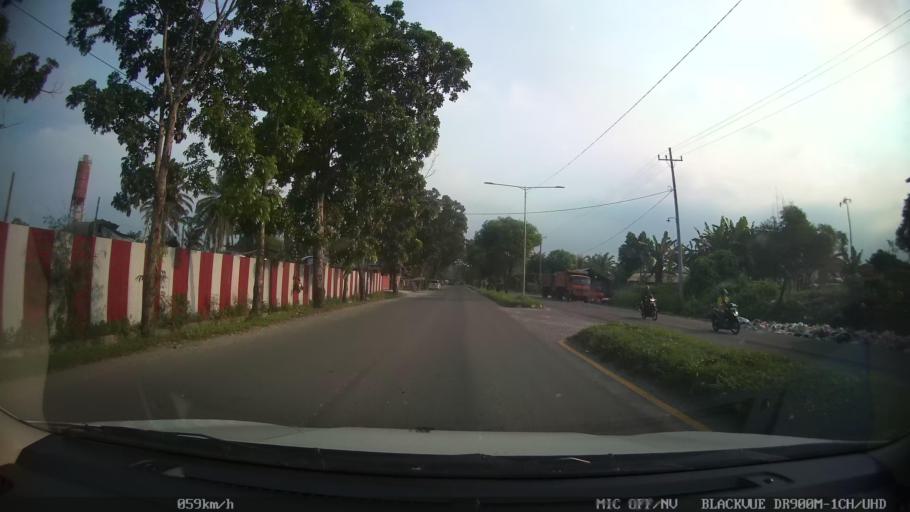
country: ID
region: North Sumatra
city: Binjai
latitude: 3.6115
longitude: 98.5343
